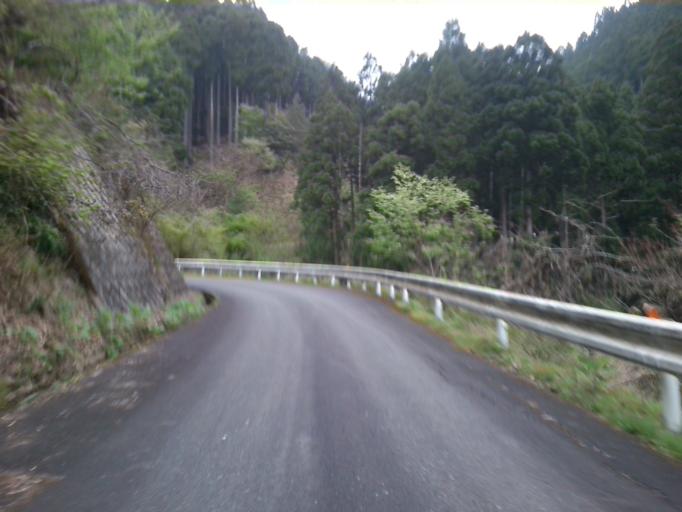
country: JP
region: Kyoto
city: Maizuru
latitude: 35.3843
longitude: 135.4385
